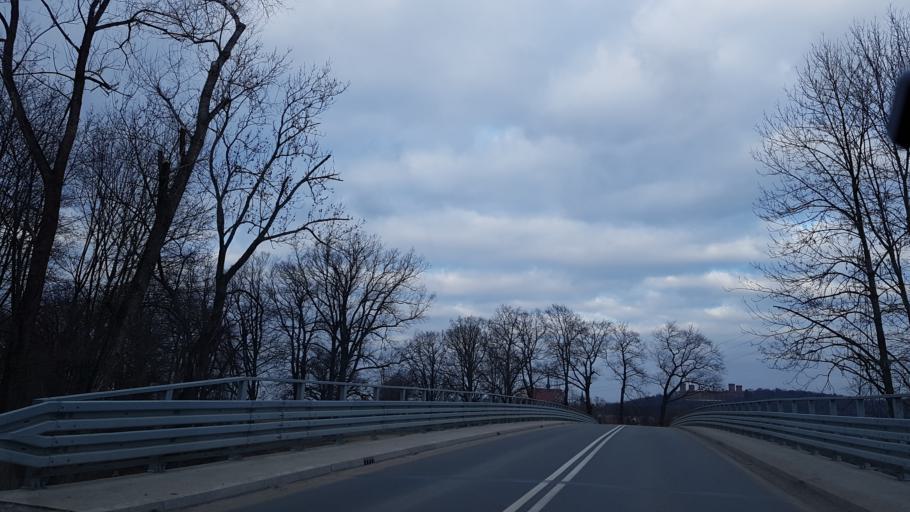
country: PL
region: Lower Silesian Voivodeship
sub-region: Powiat zabkowicki
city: Kamieniec Zabkowicki
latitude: 50.5124
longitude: 16.8697
